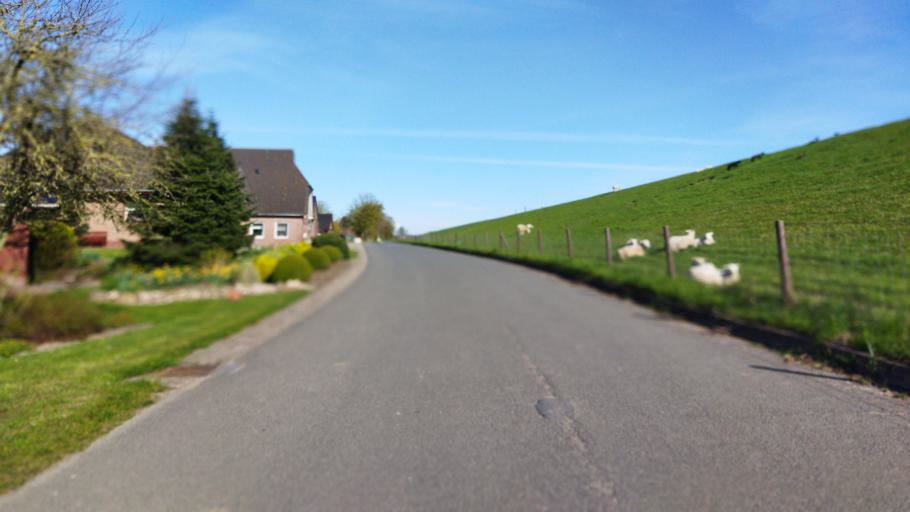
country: DE
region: Lower Saxony
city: Elsfleth
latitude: 53.2173
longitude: 8.4760
